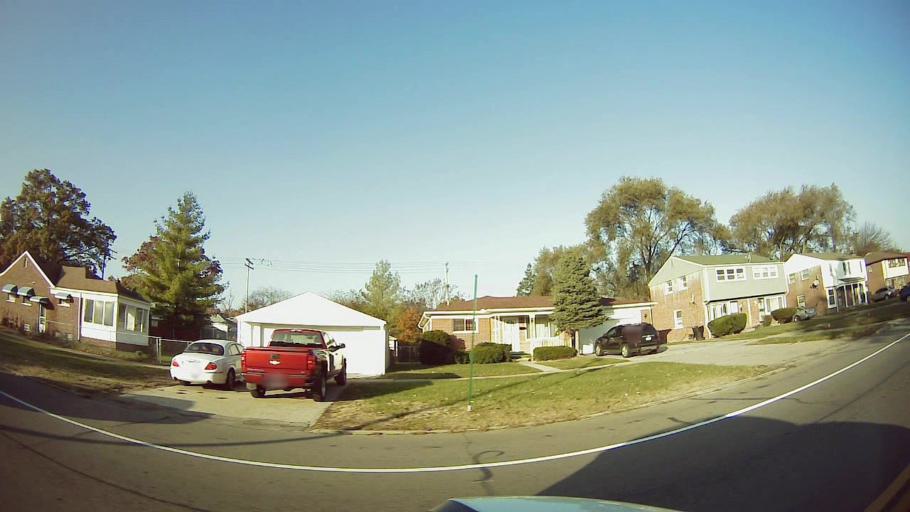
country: US
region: Michigan
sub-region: Oakland County
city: Oak Park
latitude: 42.4355
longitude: -83.1610
